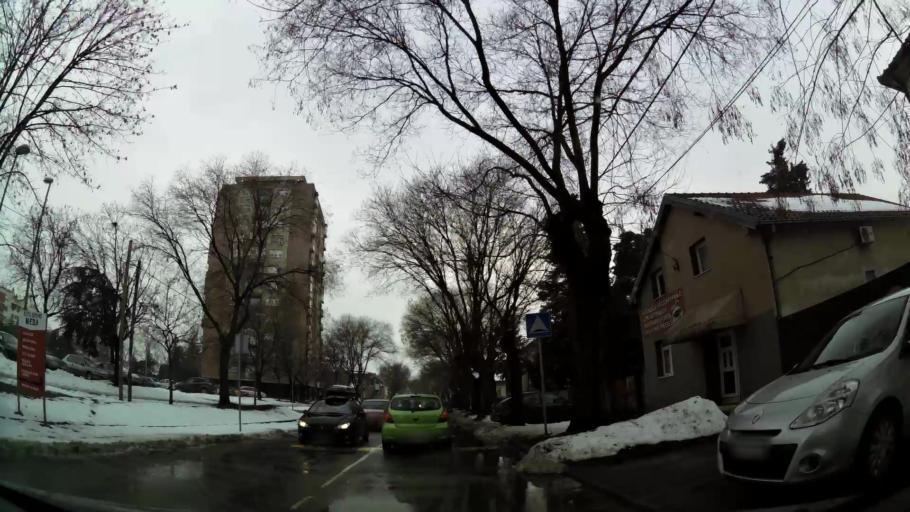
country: RS
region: Central Serbia
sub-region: Belgrade
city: Zemun
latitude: 44.8379
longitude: 20.3923
